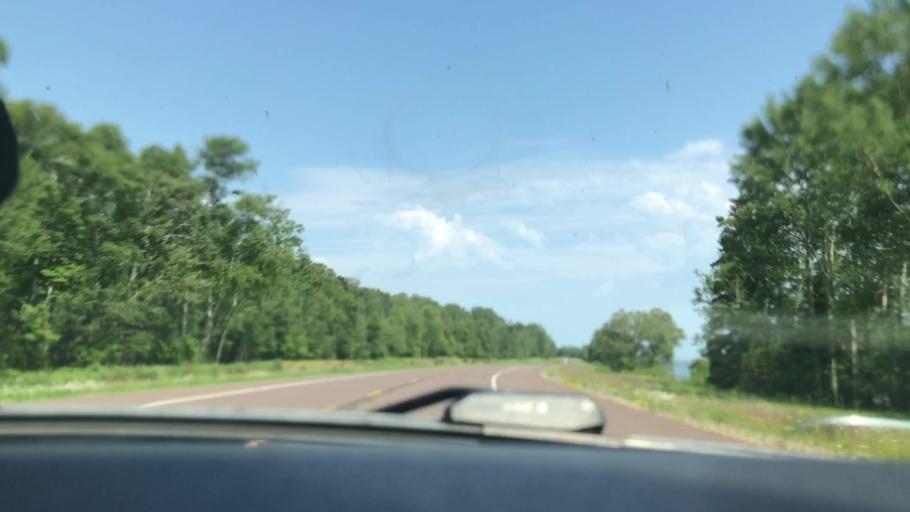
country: US
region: Minnesota
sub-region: Cook County
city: Grand Marais
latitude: 47.7777
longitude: -90.2159
